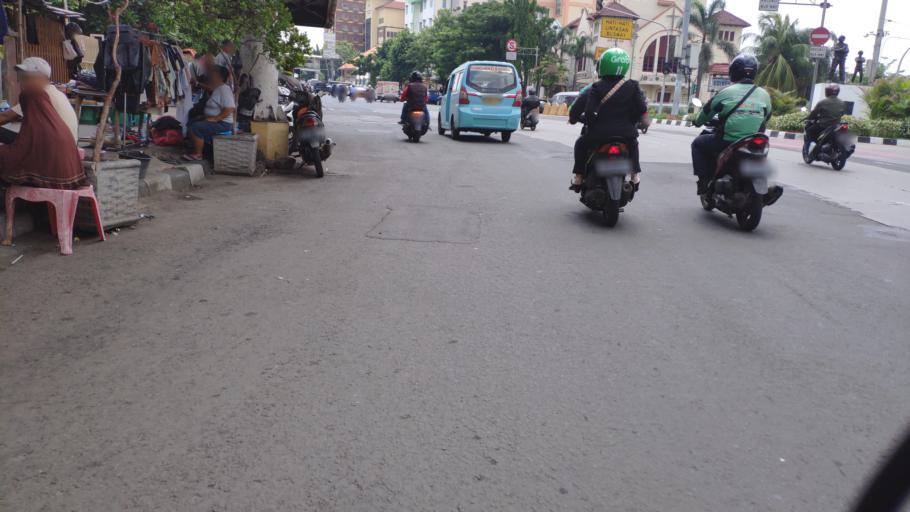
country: ID
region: Jakarta Raya
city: Jakarta
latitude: -6.2131
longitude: 106.8614
